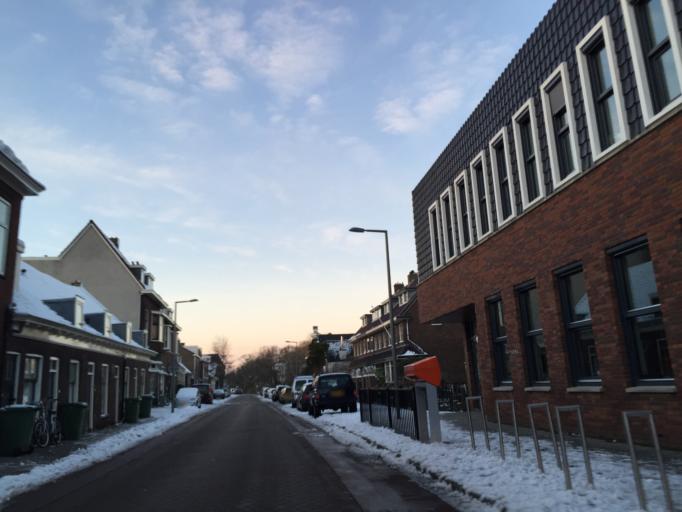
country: NL
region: South Holland
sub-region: Gemeente Schiedam
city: Schiedam
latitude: 51.9420
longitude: 4.4212
